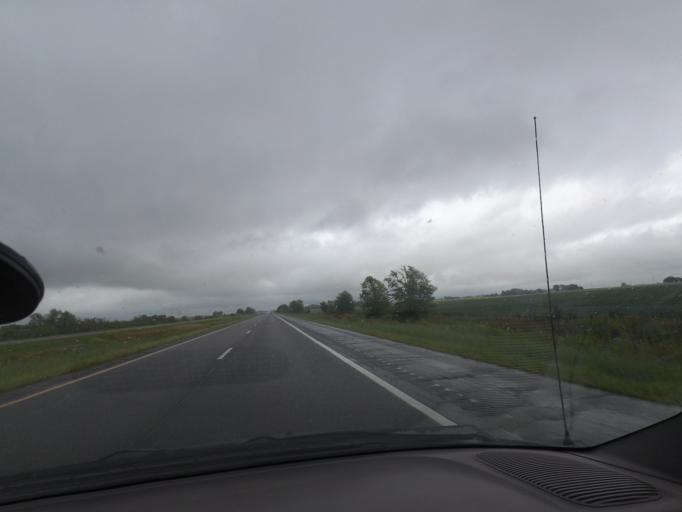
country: US
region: Illinois
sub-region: Champaign County
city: Mahomet
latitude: 40.1203
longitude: -88.4241
